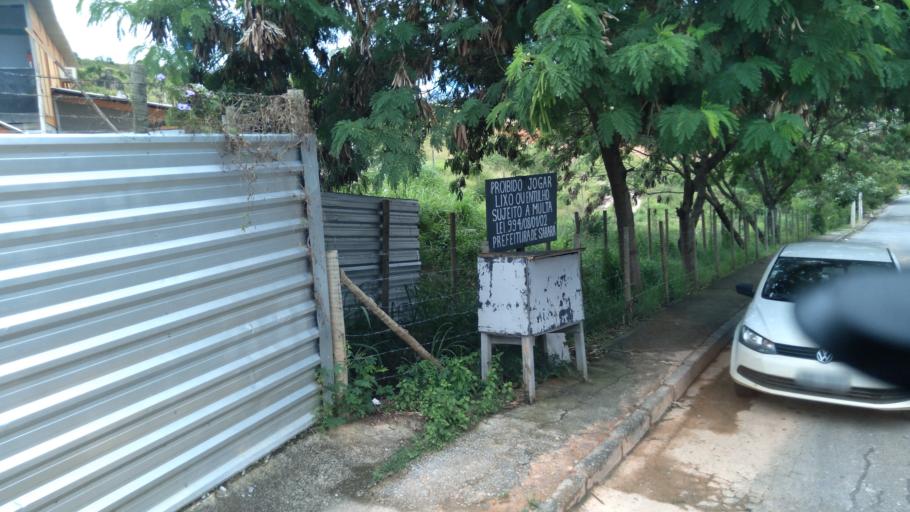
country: BR
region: Minas Gerais
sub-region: Belo Horizonte
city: Belo Horizonte
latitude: -19.8956
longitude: -43.8859
